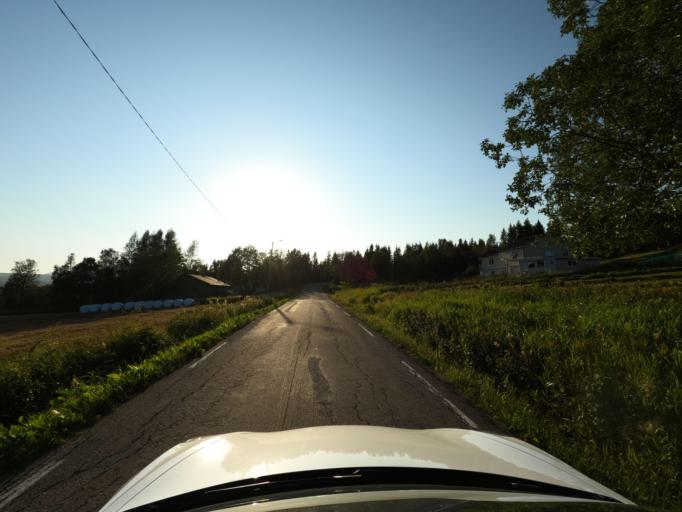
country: NO
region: Nordland
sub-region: Ballangen
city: Ballangen
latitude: 68.4942
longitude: 16.7371
